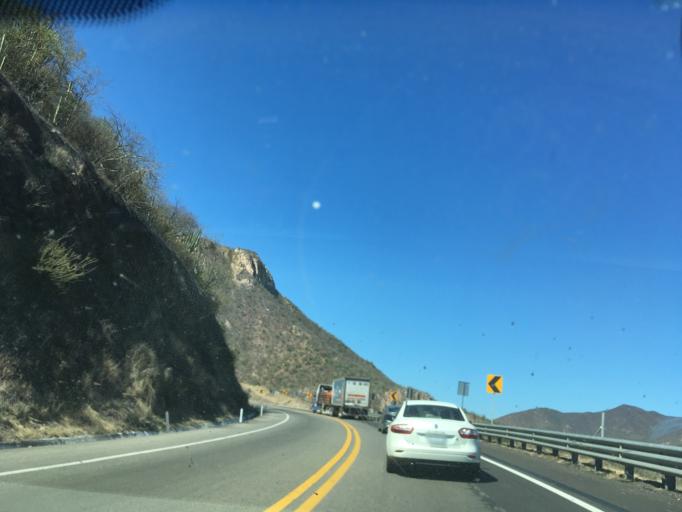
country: MX
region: Michoacan
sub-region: Arteaga
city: Las Canas
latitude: 18.4517
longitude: -101.9281
